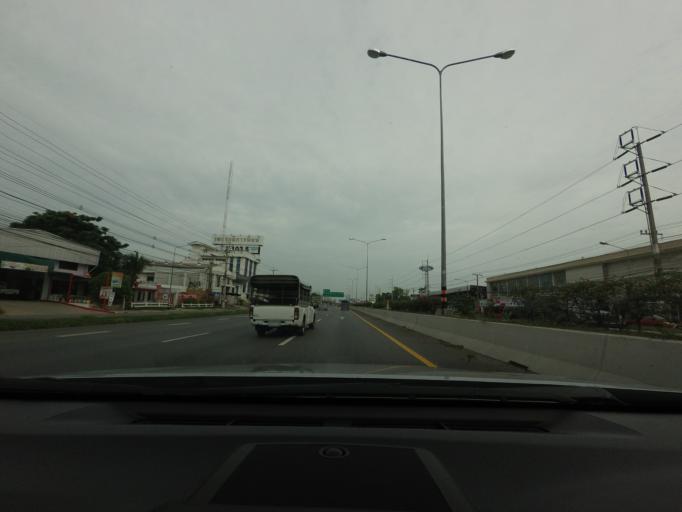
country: TH
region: Phetchaburi
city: Phetchaburi
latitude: 13.0961
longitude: 99.9388
